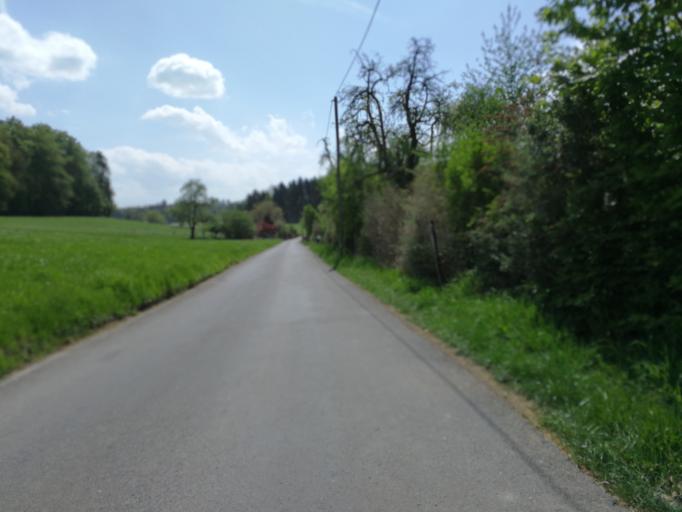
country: CH
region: Zurich
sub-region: Bezirk Hinwil
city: Binzikon
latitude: 47.2840
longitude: 8.7467
